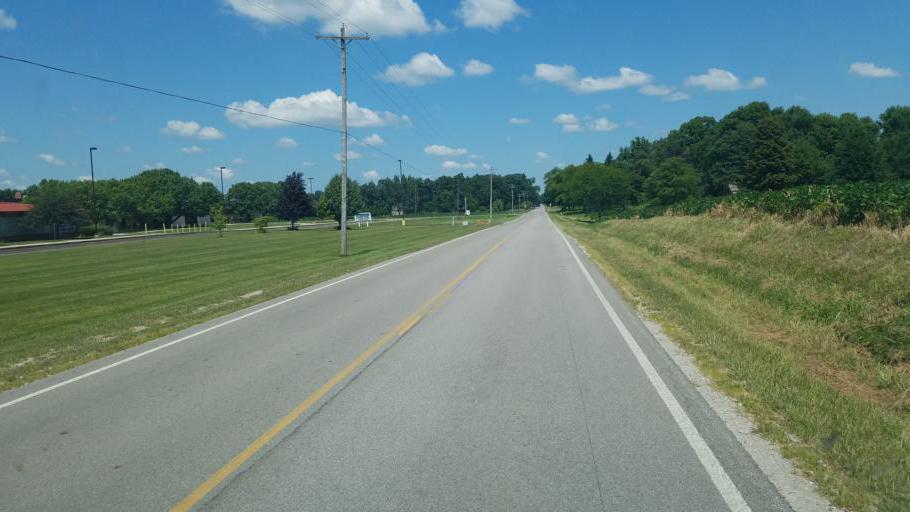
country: US
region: Ohio
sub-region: Marion County
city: Marion
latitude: 40.6479
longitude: -83.1733
